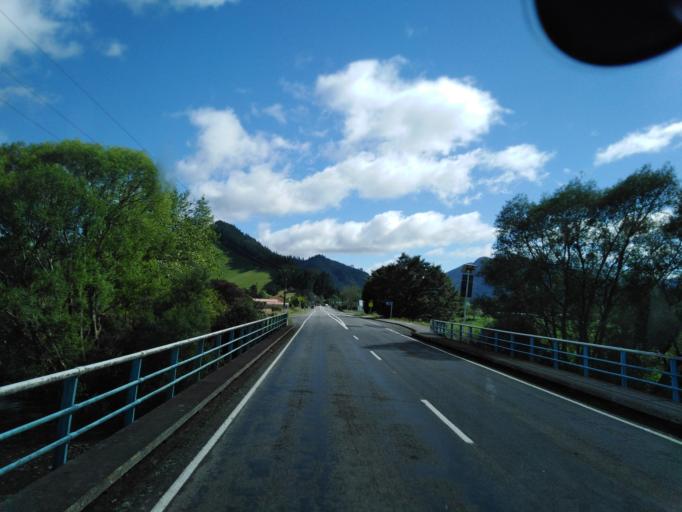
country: NZ
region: Nelson
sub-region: Nelson City
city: Nelson
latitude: -41.2327
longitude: 173.5815
